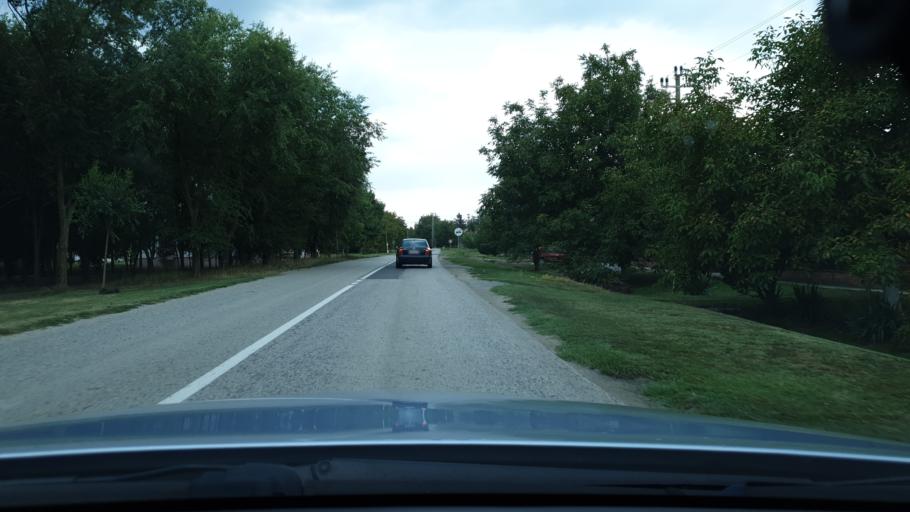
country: RS
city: Konak
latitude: 45.3172
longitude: 20.9074
